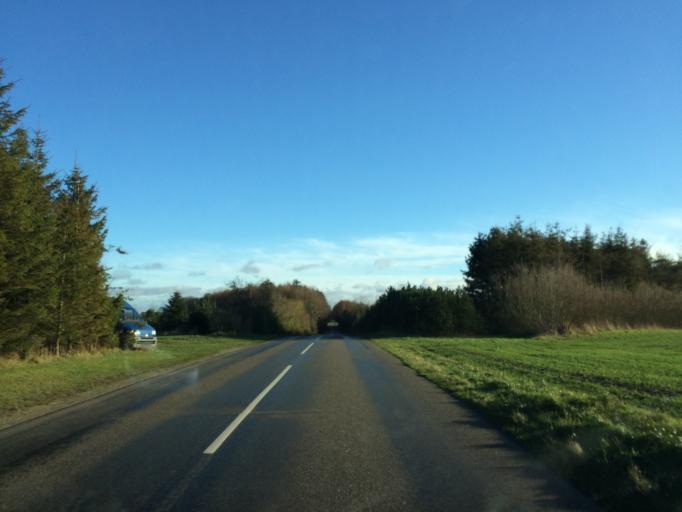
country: DK
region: Central Jutland
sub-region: Herning Kommune
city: Kibaek
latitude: 56.0566
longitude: 8.7797
